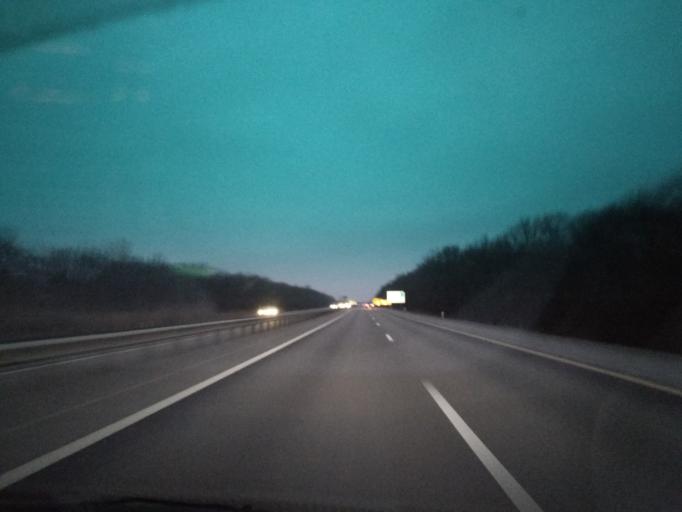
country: RU
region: Krasnodarskiy
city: Saratovskaya
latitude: 44.7756
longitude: 39.2332
